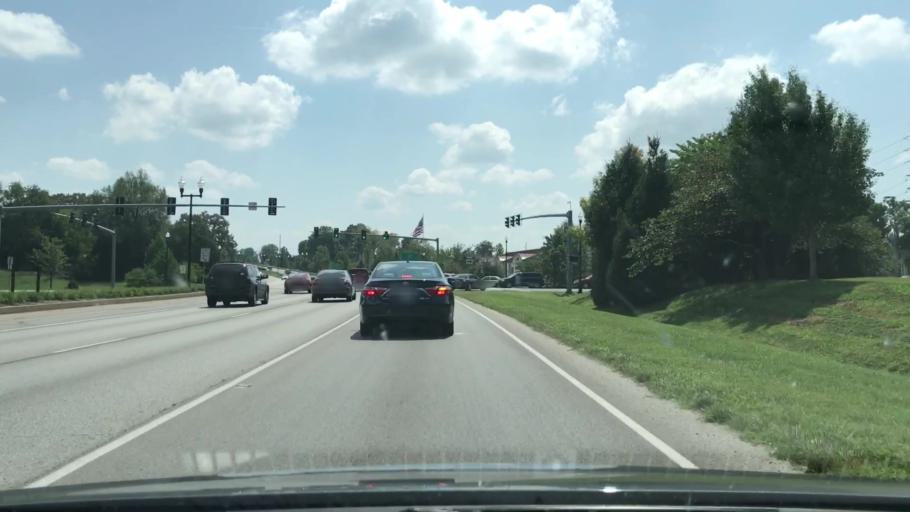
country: US
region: Kentucky
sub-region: Warren County
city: Bowling Green
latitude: 36.9818
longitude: -86.3967
